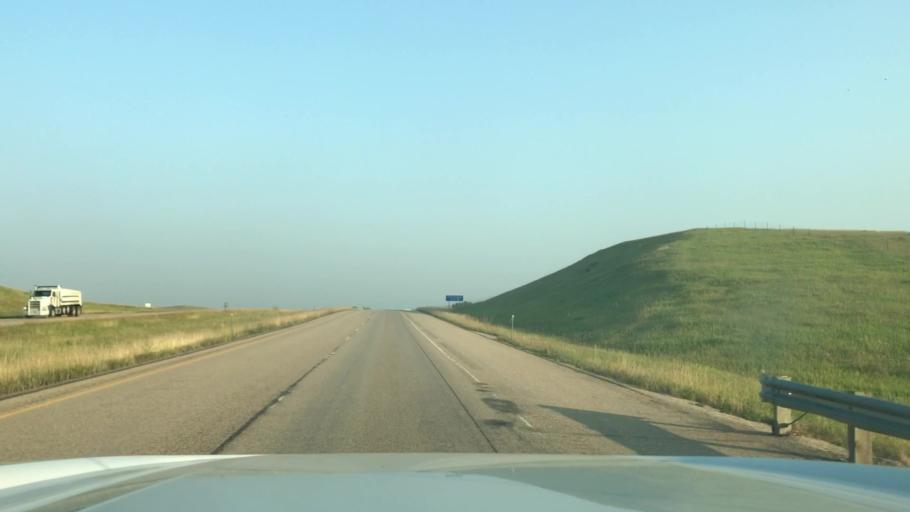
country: US
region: Wyoming
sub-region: Sheridan County
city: Sheridan
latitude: 45.0110
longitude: -107.3031
